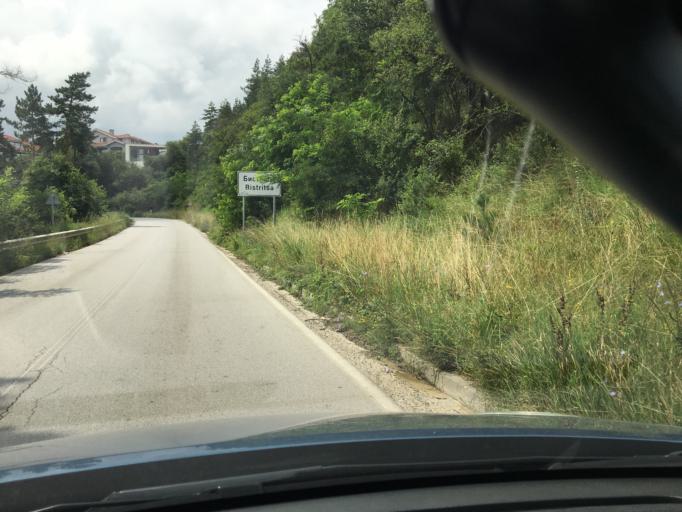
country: BG
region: Sofia-Capital
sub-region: Stolichna Obshtina
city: Sofia
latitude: 42.6008
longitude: 23.3685
